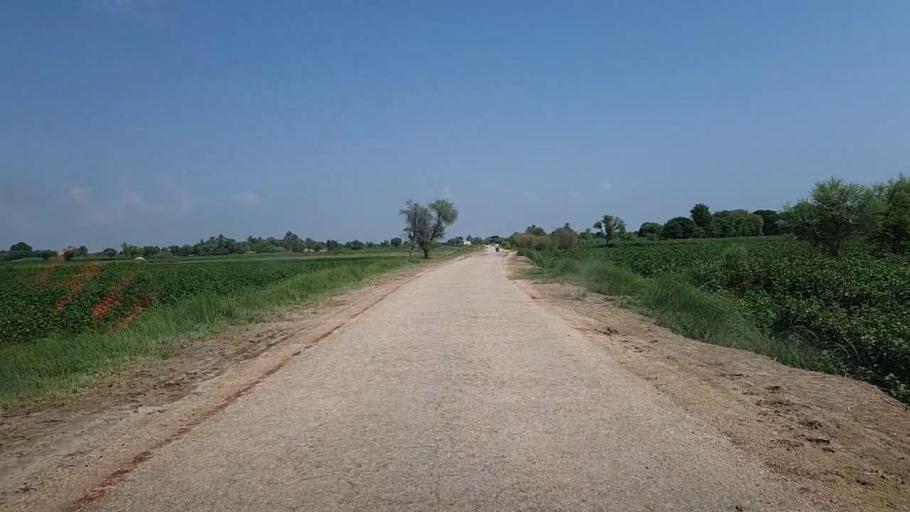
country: PK
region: Sindh
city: Bhiria
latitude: 26.8908
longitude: 68.2276
